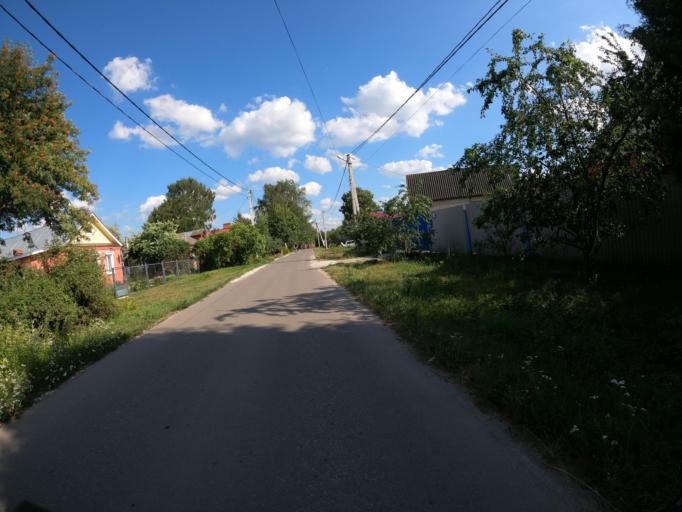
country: RU
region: Moskovskaya
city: Peski
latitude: 55.2104
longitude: 38.7381
